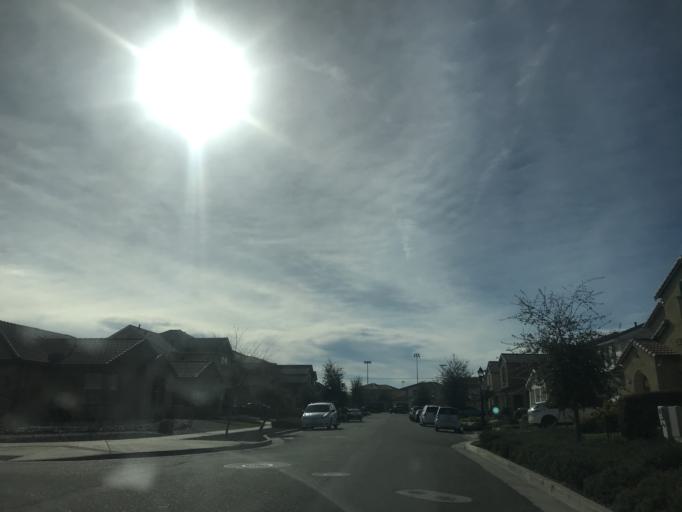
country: US
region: California
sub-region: Yolo County
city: Woodland
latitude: 38.6575
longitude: -121.7607
